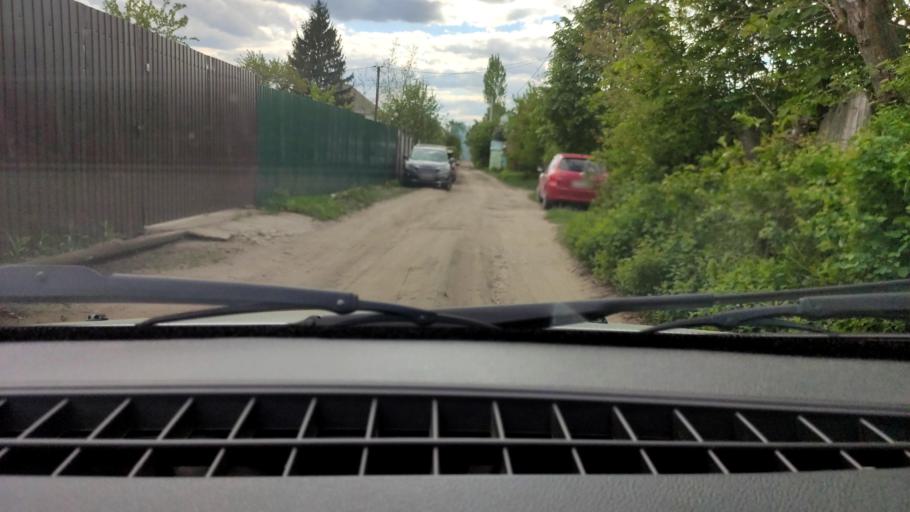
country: RU
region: Voronezj
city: Shilovo
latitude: 51.5987
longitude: 39.1444
